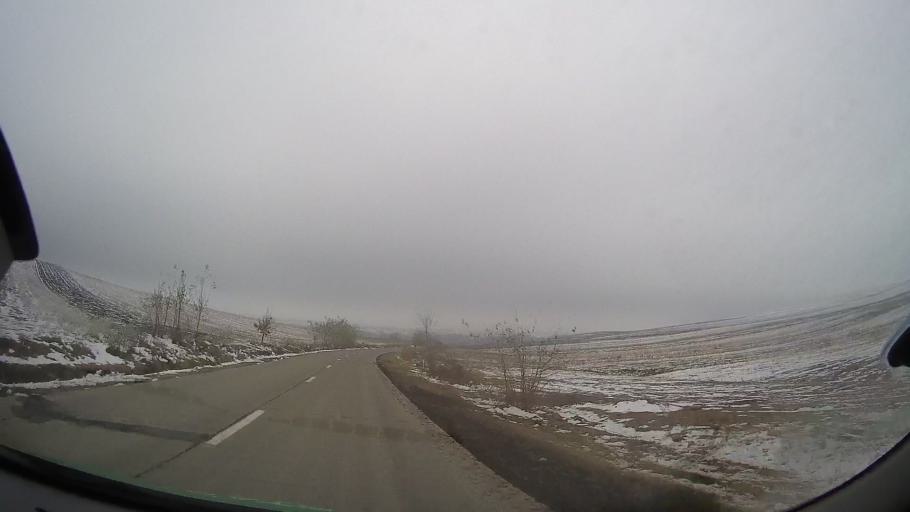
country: RO
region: Vaslui
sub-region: Comuna Ivesti
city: Ivesti
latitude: 46.1991
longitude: 27.5131
